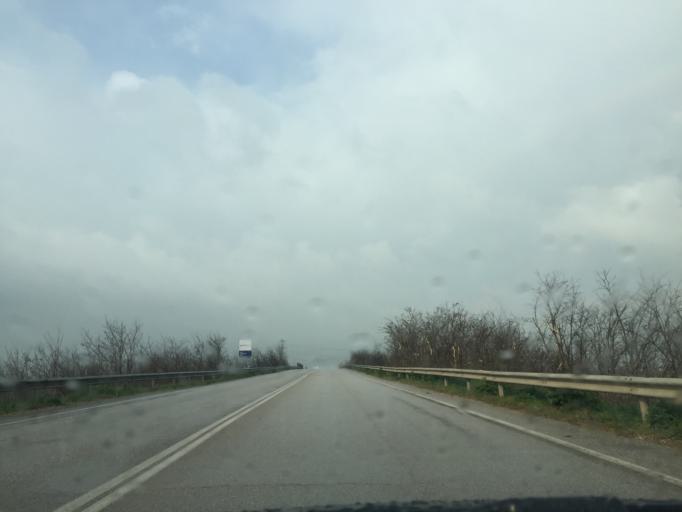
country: IT
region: Apulia
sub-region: Provincia di Foggia
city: Foggia
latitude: 41.4982
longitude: 15.5347
